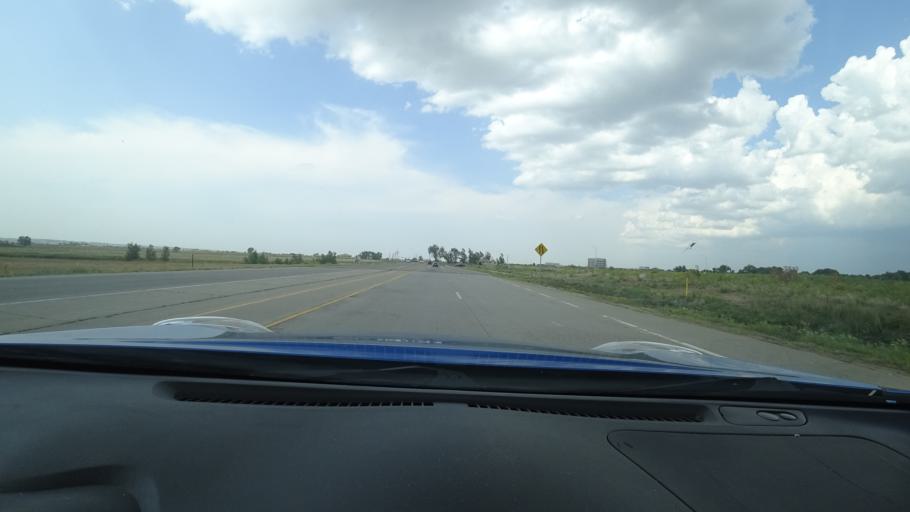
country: US
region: Colorado
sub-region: Adams County
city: Brighton
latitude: 39.9168
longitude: -104.8186
